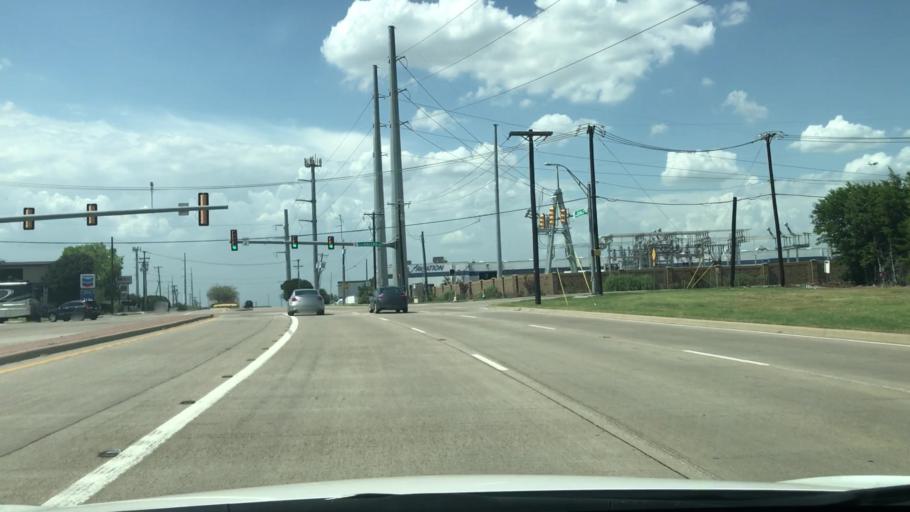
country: US
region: Texas
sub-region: Tarrant County
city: Grapevine
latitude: 32.9320
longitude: -97.0607
